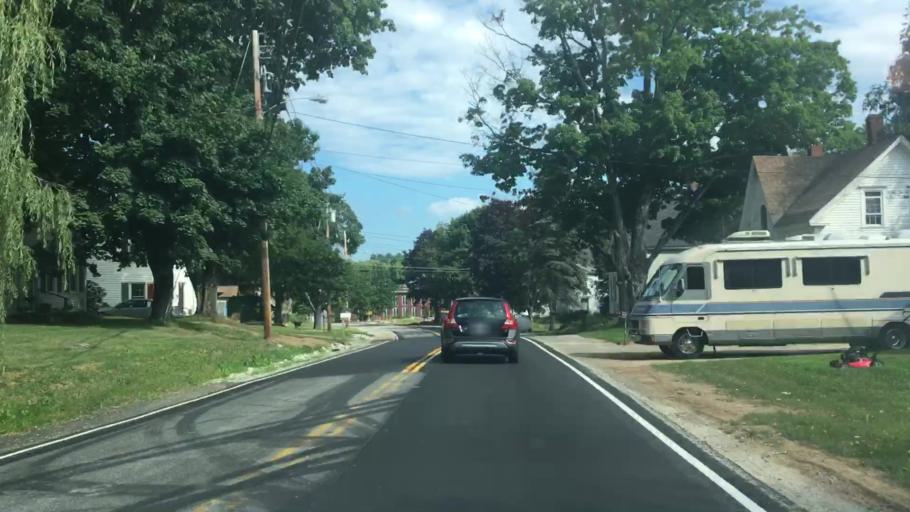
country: US
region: Maine
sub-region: Oxford County
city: Oxford
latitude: 44.1324
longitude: -70.4975
